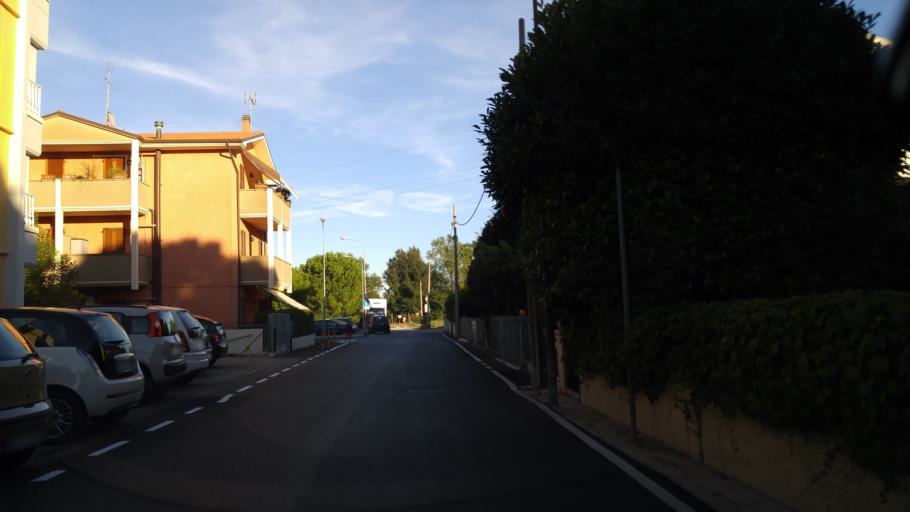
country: IT
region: The Marches
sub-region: Provincia di Pesaro e Urbino
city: Fano
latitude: 43.8353
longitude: 13.0179
